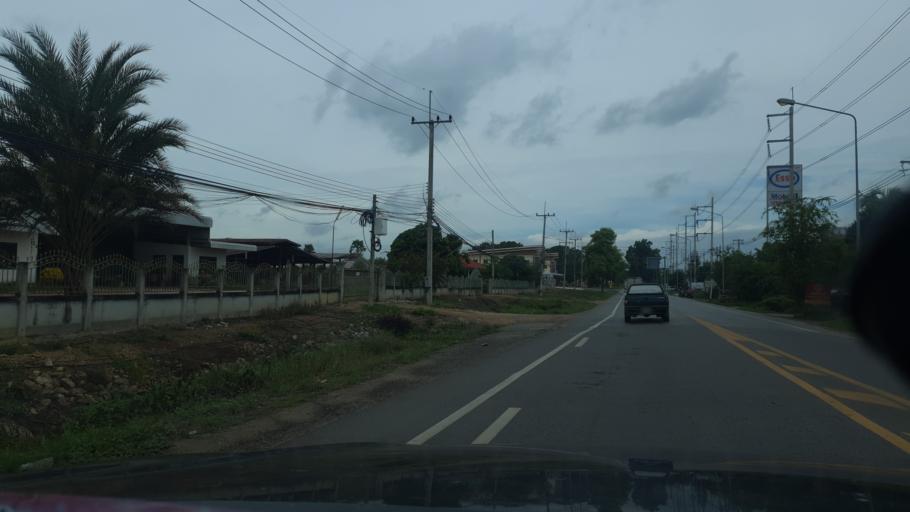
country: TH
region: Lamphun
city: Pa Sang
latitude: 18.4725
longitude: 98.9533
